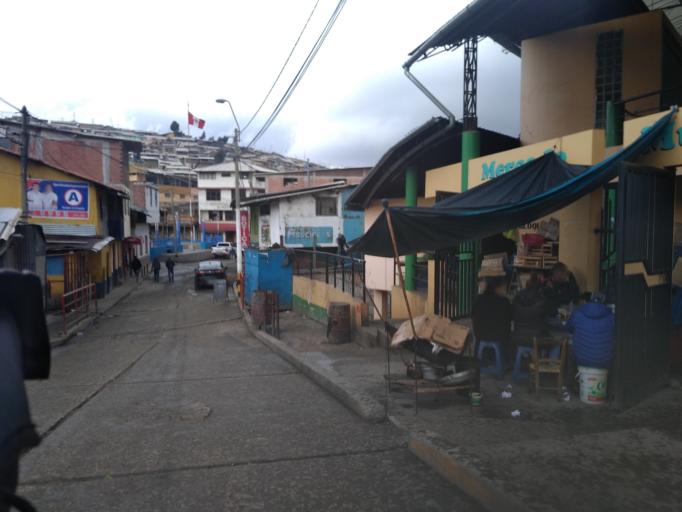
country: PE
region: La Libertad
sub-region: Provincia de Santiago de Chuco
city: Quiruvilca
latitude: -8.0011
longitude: -78.3100
